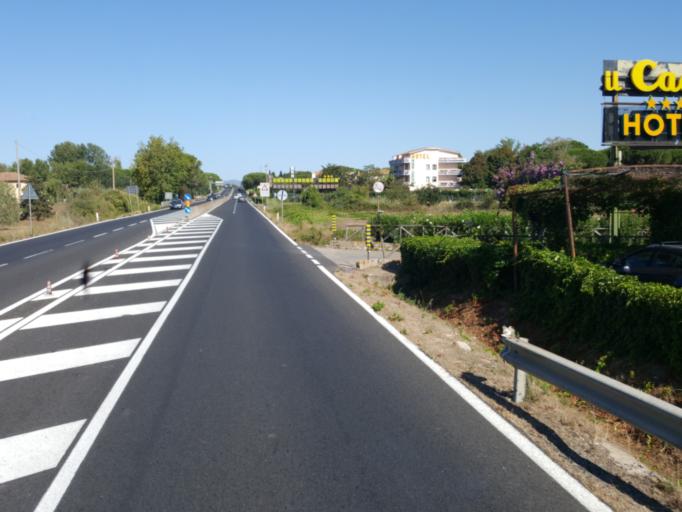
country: IT
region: Tuscany
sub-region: Provincia di Grosseto
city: Orbetello Scalo
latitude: 42.4726
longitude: 11.2351
